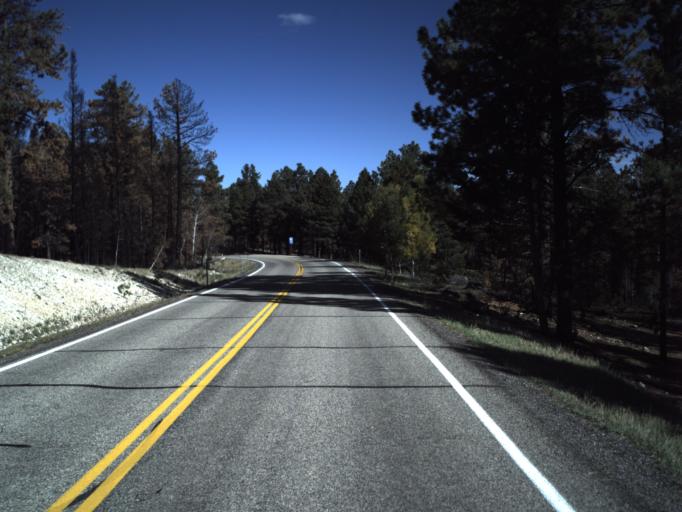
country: US
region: Utah
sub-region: Iron County
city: Parowan
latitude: 37.6548
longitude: -112.6829
